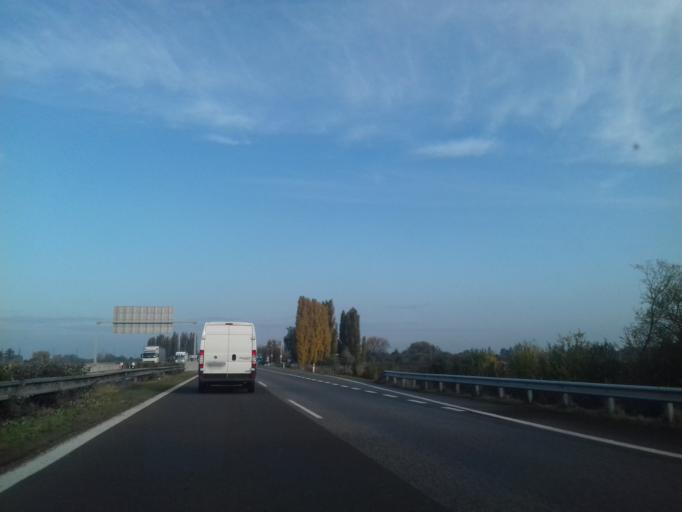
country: SK
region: Bratislavsky
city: Stupava
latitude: 48.2568
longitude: 17.0108
